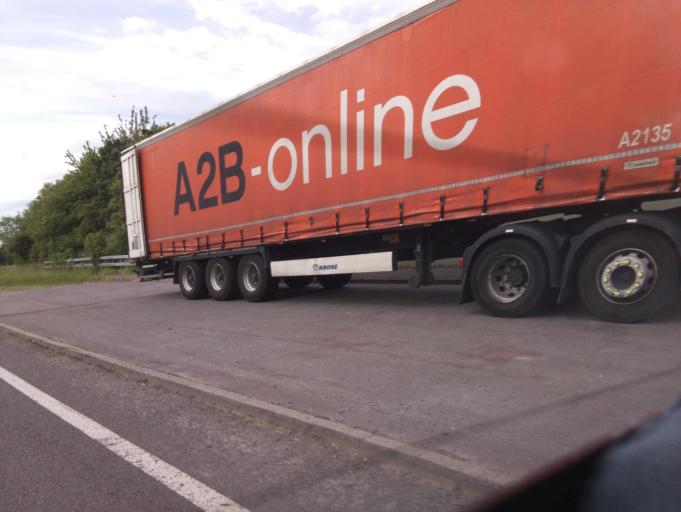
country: GB
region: England
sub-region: Worcestershire
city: Worcester
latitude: 52.1825
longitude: -2.2610
